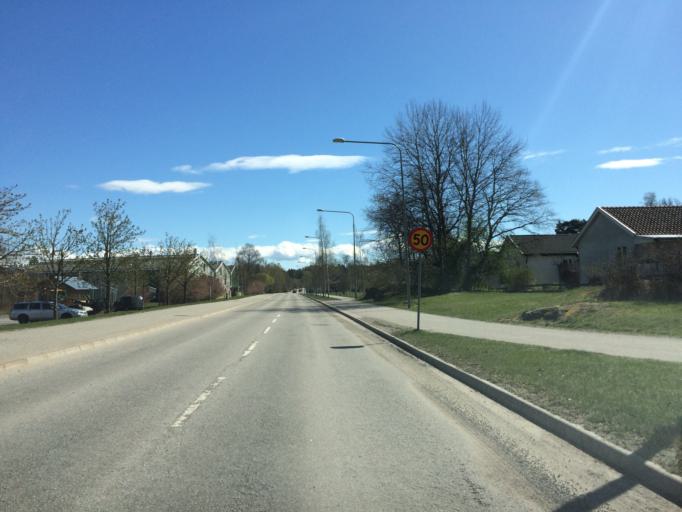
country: SE
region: Stockholm
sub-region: Huddinge Kommun
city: Huddinge
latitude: 59.2759
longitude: 17.9818
